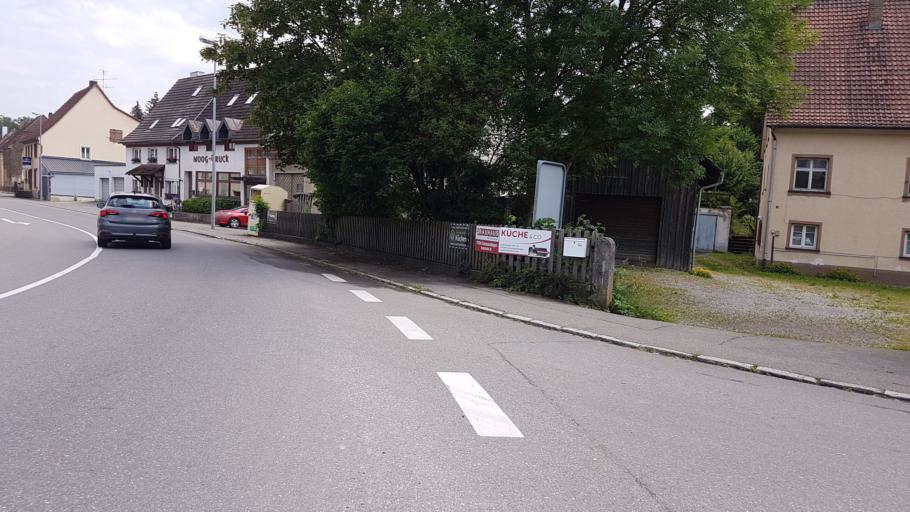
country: DE
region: Baden-Wuerttemberg
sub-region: Freiburg Region
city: Hufingen
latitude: 47.9224
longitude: 8.4888
